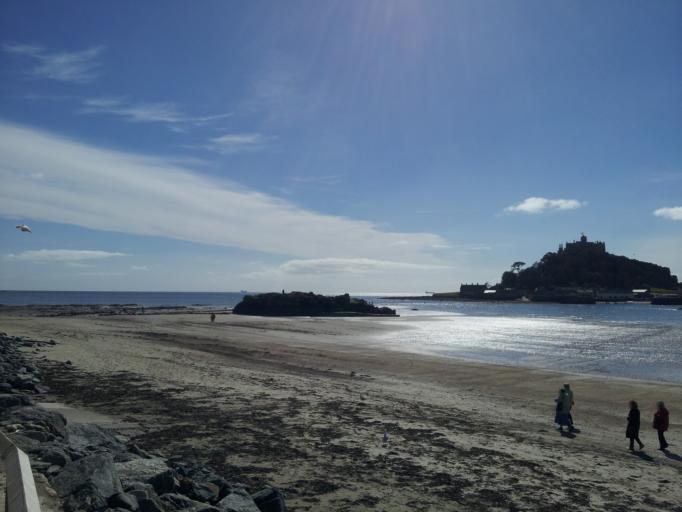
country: GB
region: England
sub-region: Cornwall
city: Marazion
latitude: 50.1240
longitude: -5.4763
